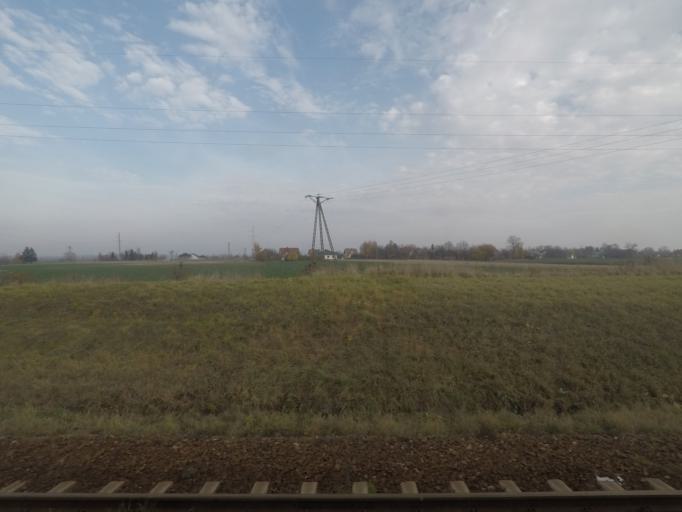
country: PL
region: Subcarpathian Voivodeship
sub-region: Powiat jaroslawski
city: Radymno
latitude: 49.9294
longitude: 22.8391
